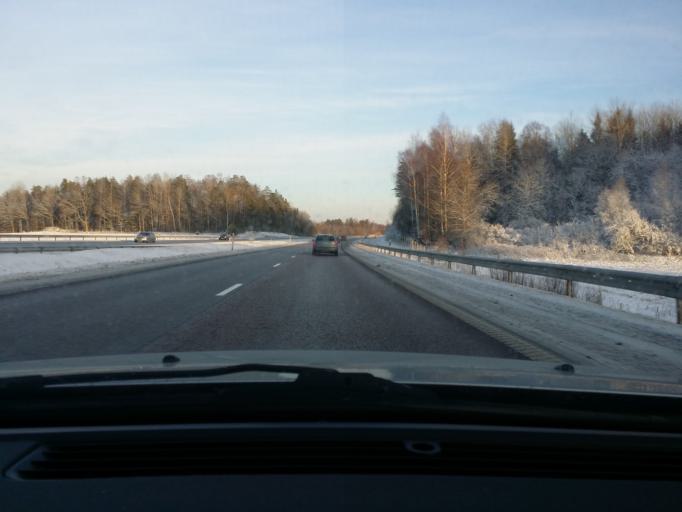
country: SE
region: OErebro
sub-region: Lindesbergs Kommun
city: Fellingsbro
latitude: 59.3208
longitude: 15.4765
